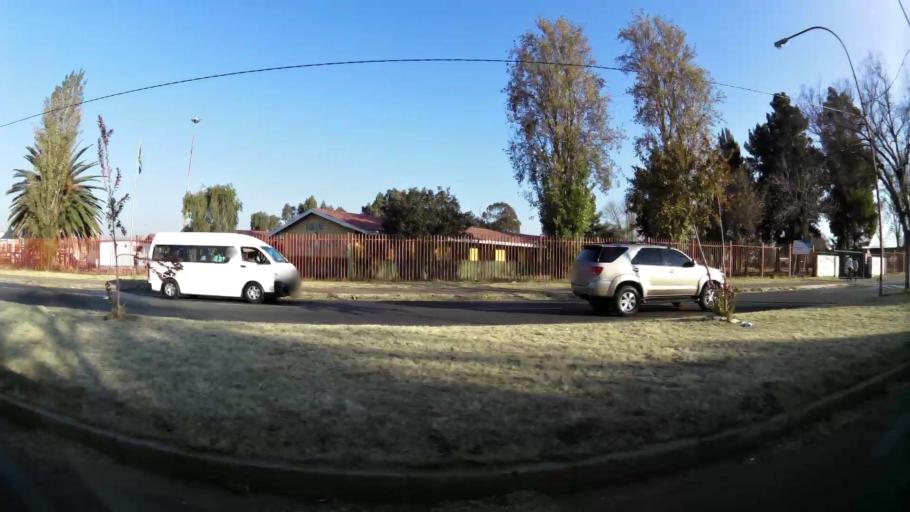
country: ZA
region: Gauteng
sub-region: City of Johannesburg Metropolitan Municipality
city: Soweto
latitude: -26.2521
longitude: 27.8798
